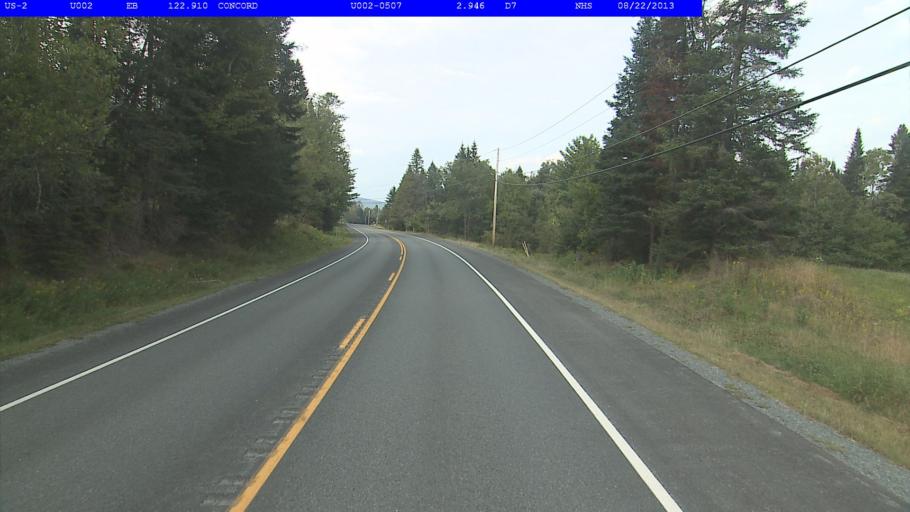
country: US
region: Vermont
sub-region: Caledonia County
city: St Johnsbury
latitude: 44.4368
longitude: -71.8787
